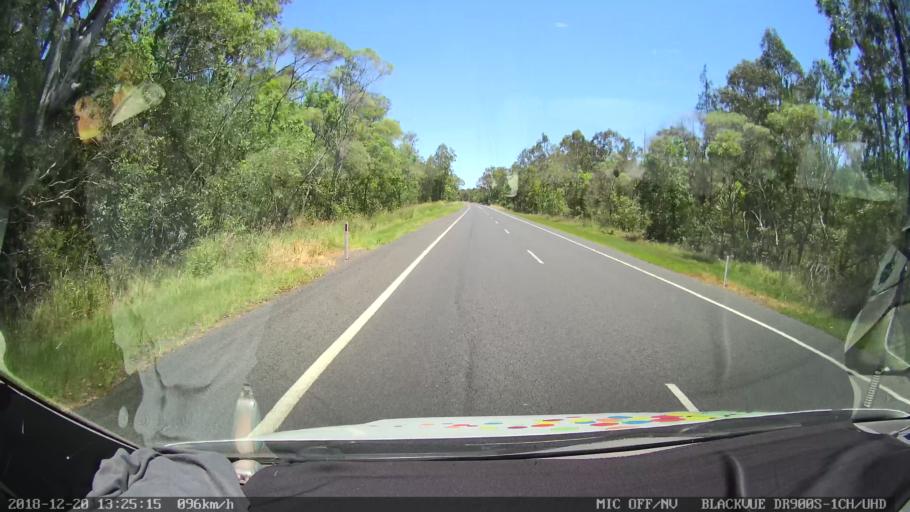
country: AU
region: New South Wales
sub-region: Richmond Valley
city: Casino
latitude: -29.1285
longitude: 152.9971
